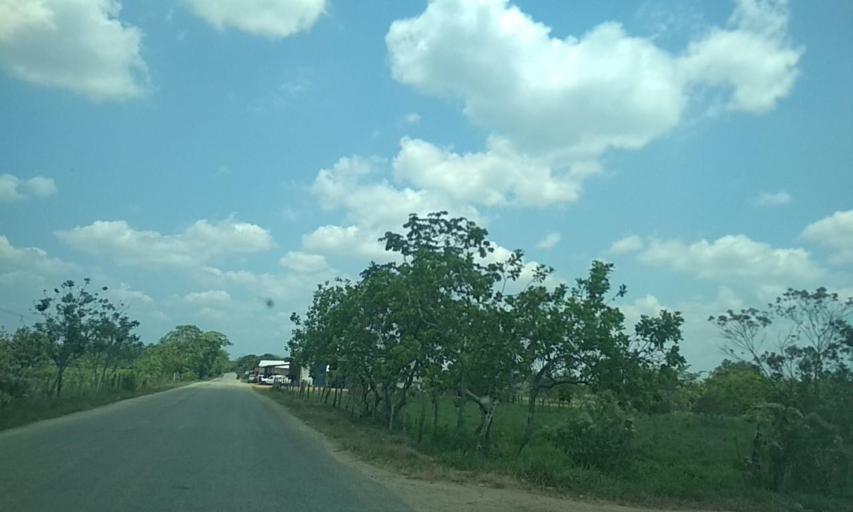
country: MX
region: Tabasco
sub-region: Huimanguillo
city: Francisco Rueda
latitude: 17.7739
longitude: -93.8138
